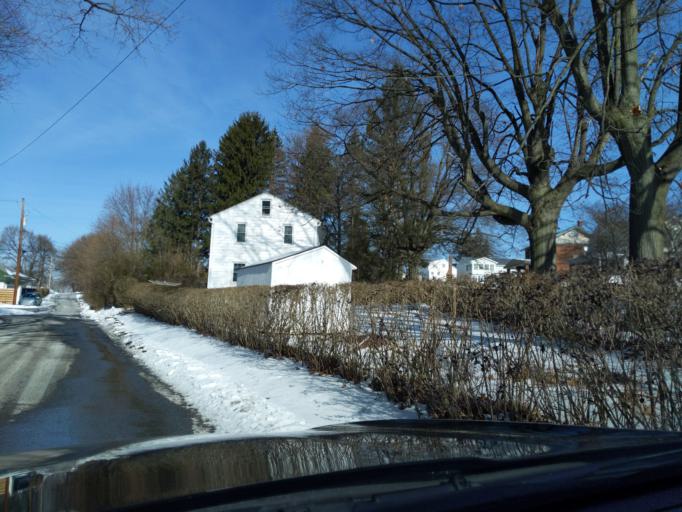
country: US
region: Pennsylvania
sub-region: Blair County
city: Greenwood
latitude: 40.5238
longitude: -78.3729
